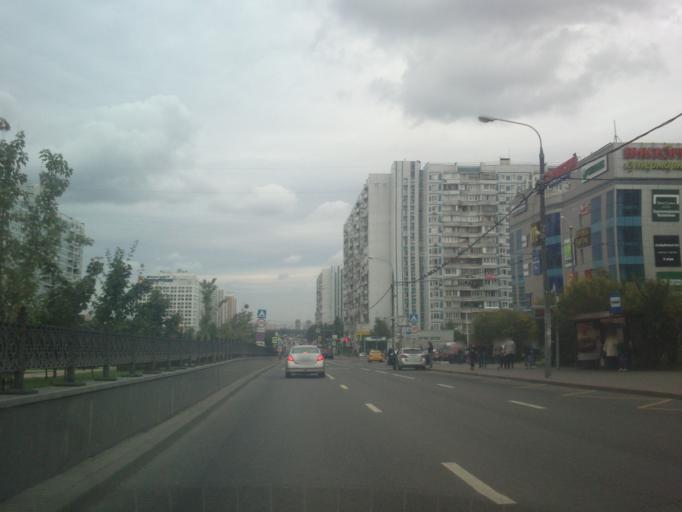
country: RU
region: Moskovskaya
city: Bol'shaya Setun'
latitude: 55.7583
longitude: 37.4084
